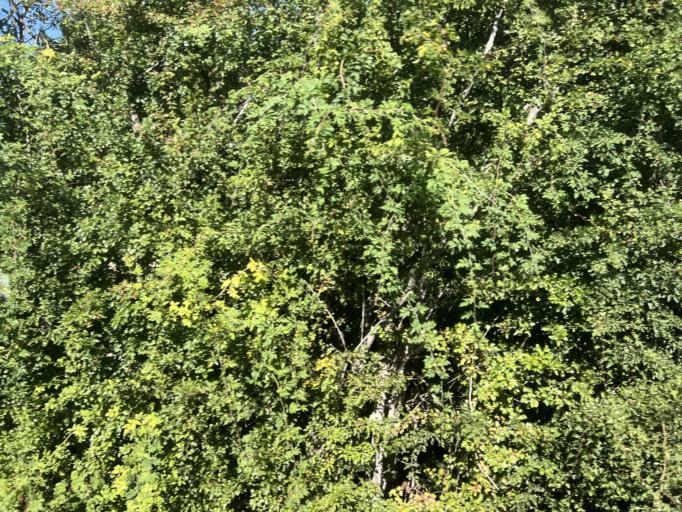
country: GB
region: England
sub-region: Lincolnshire
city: Boston
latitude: 53.0559
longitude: 0.0534
